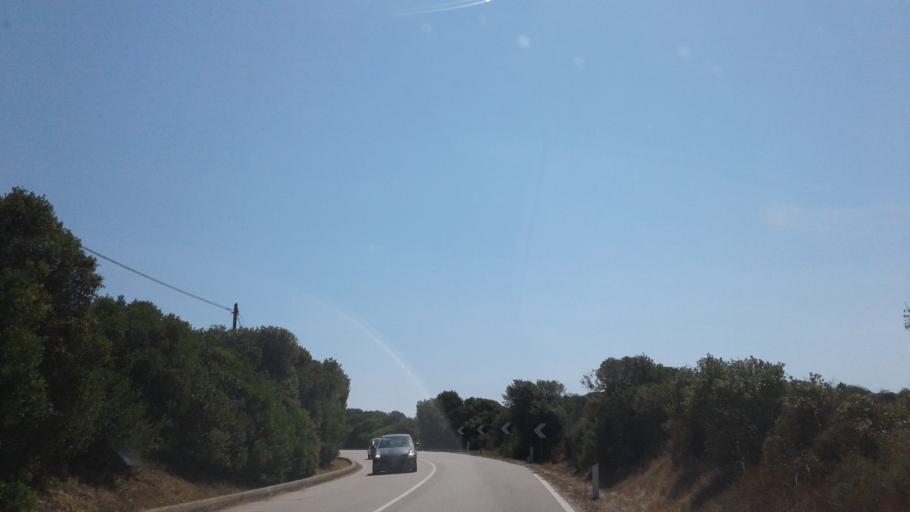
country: IT
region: Sardinia
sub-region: Provincia di Olbia-Tempio
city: Luogosanto
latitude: 41.1266
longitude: 9.2807
